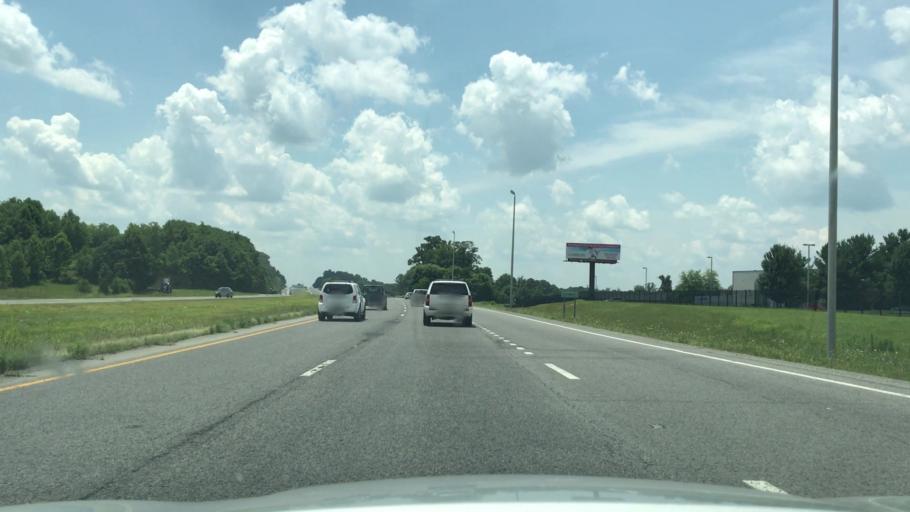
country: US
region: Tennessee
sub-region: Putnam County
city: Cookeville
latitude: 36.1484
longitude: -85.4763
